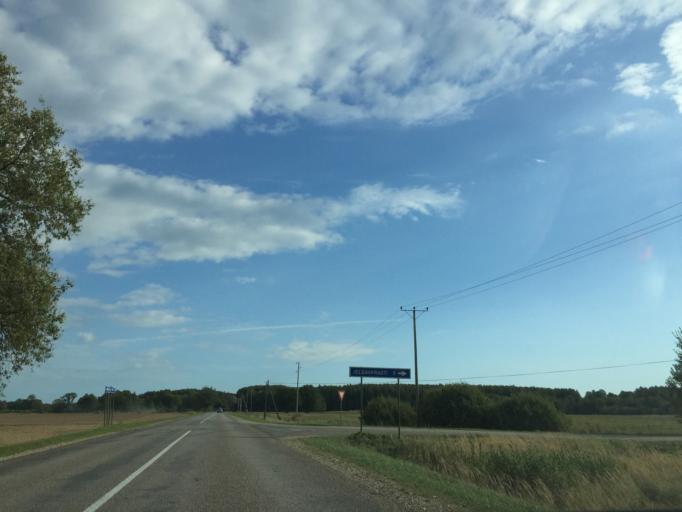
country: LV
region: Limbazu Rajons
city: Limbazi
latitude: 57.5113
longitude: 24.5143
